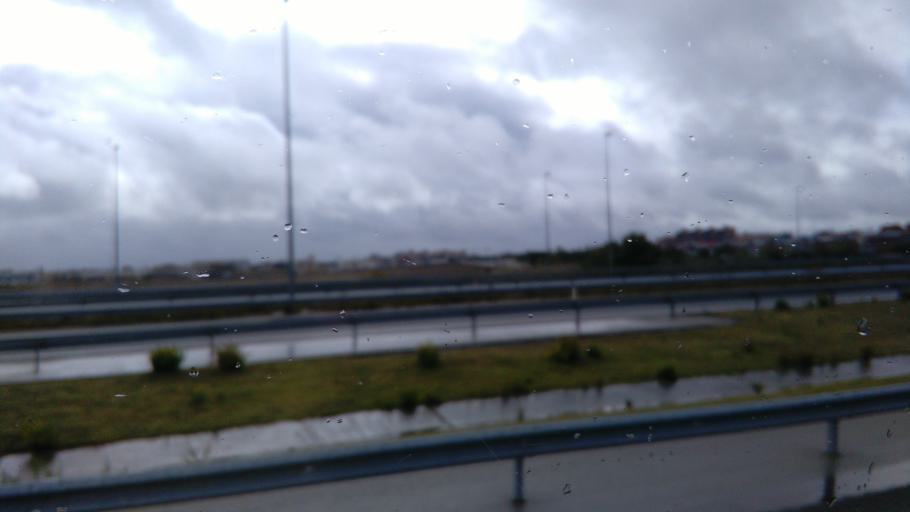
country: ES
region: Madrid
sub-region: Provincia de Madrid
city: Mostoles
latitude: 40.3095
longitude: -3.8306
